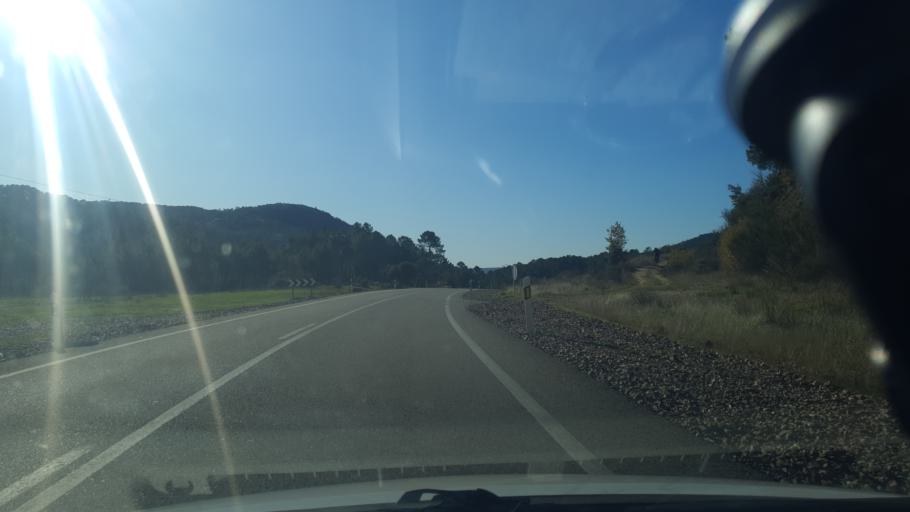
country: ES
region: Castille and Leon
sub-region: Provincia de Avila
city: Mombeltran
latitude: 40.2260
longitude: -5.0341
